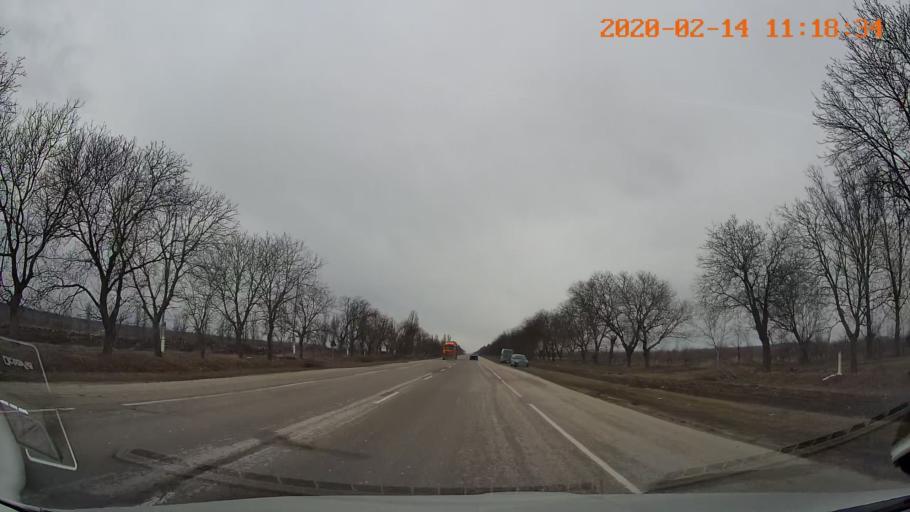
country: MD
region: Briceni
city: Briceni
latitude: 48.2669
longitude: 27.1729
